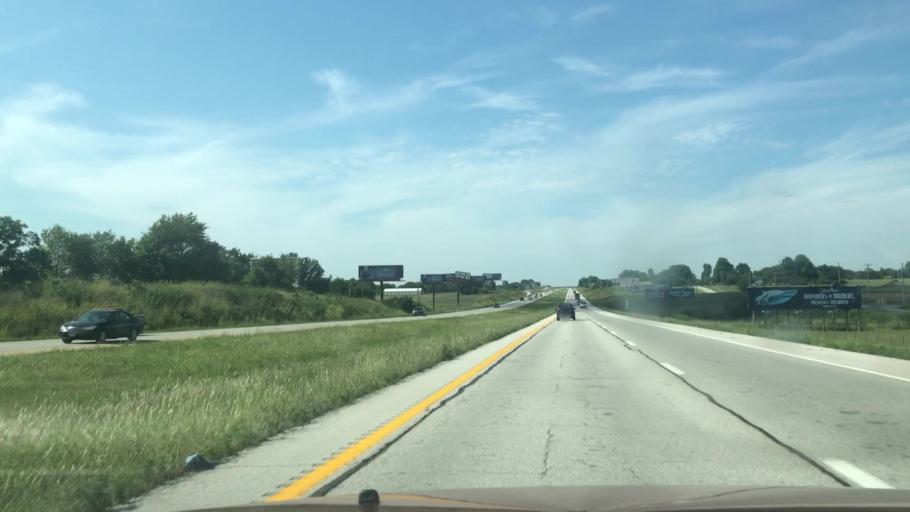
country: US
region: Missouri
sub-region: Christian County
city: Ozark
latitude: 36.9514
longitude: -93.2317
